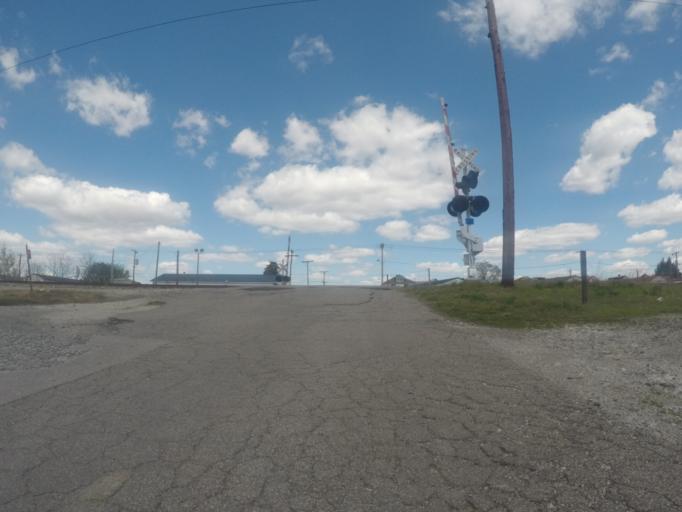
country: US
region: West Virginia
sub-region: Wayne County
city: Kenova
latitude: 38.3996
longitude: -82.5842
